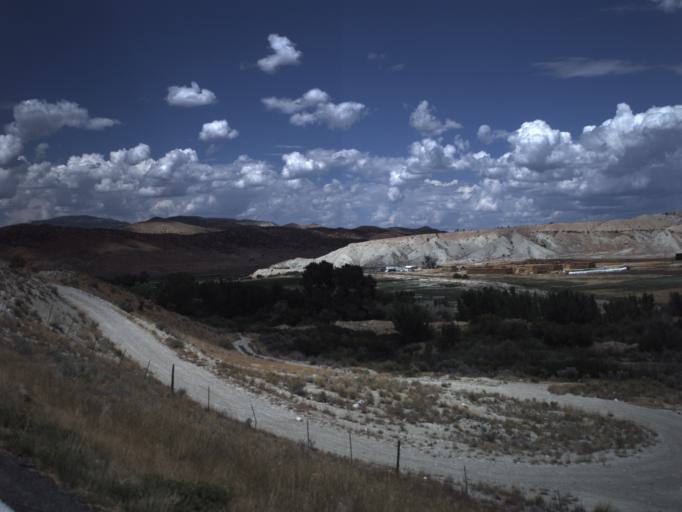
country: US
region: Utah
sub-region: Sanpete County
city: Gunnison
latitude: 39.1443
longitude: -111.7351
